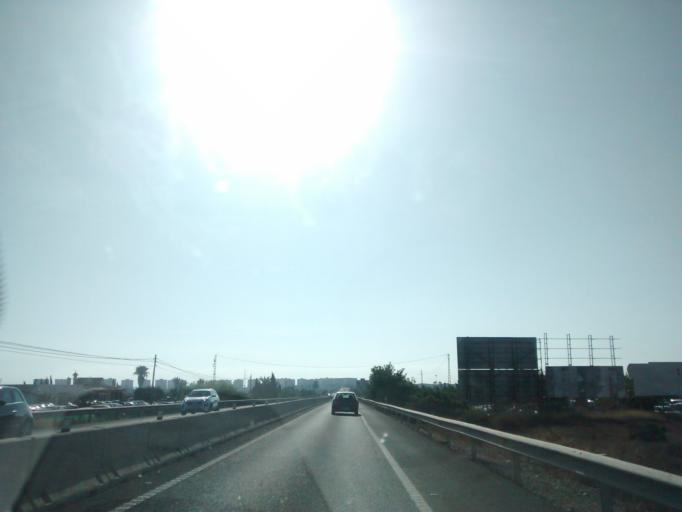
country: ES
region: Valencia
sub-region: Provincia de Alicante
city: Alicante
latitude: 38.2870
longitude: -0.5449
